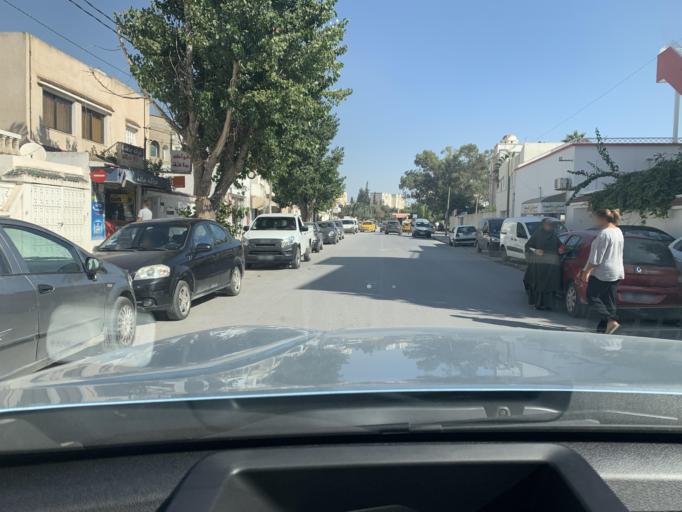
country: TN
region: Manouba
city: Manouba
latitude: 36.8260
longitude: 10.1193
